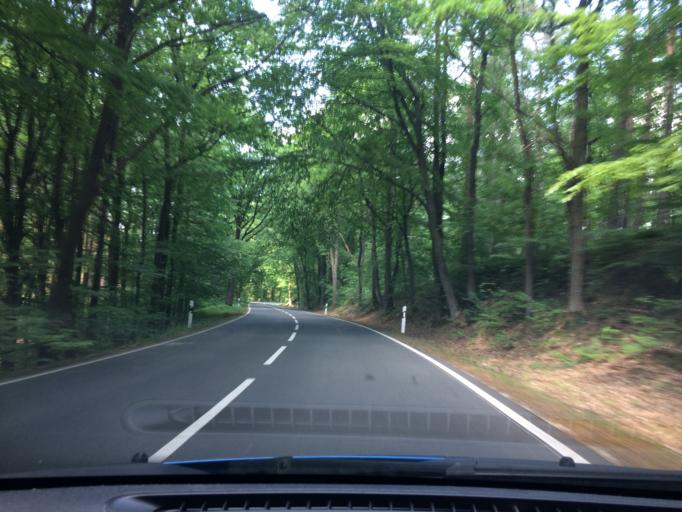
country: DE
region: Lower Saxony
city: Neu Darchau
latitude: 53.2270
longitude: 10.8692
